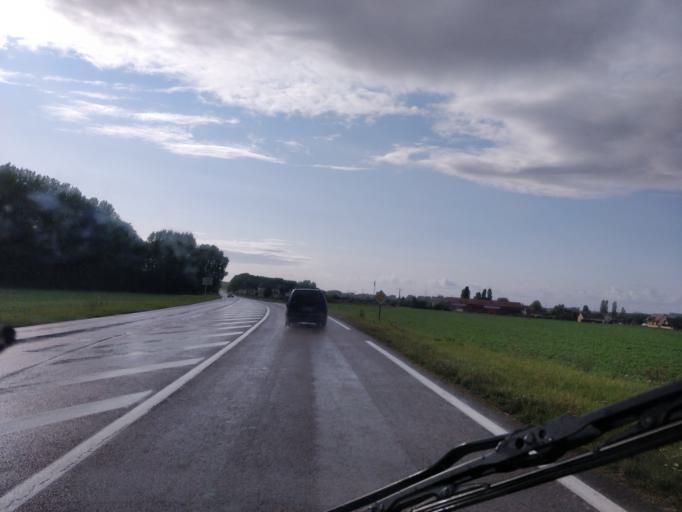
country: FR
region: Champagne-Ardenne
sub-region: Departement de l'Aube
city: Lusigny-sur-Barse
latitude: 48.2613
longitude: 4.2457
